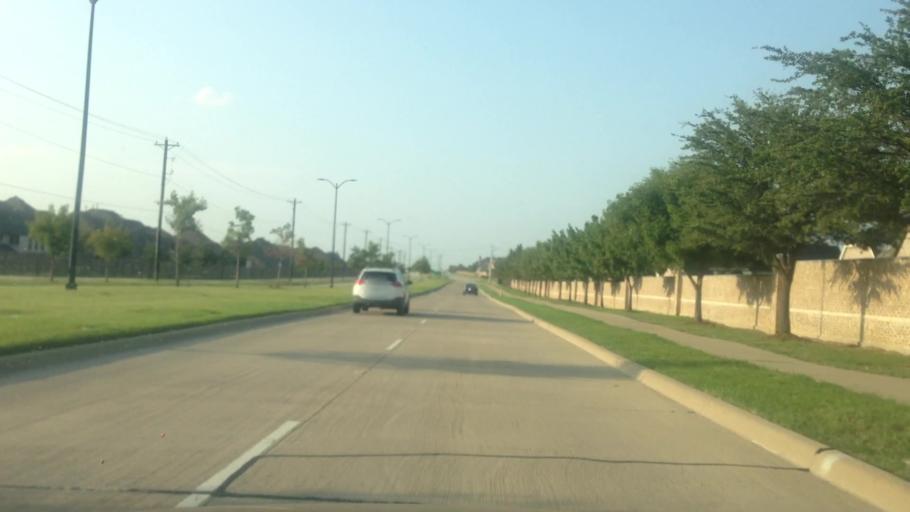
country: US
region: Texas
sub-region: Denton County
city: The Colony
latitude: 33.1265
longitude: -96.8818
